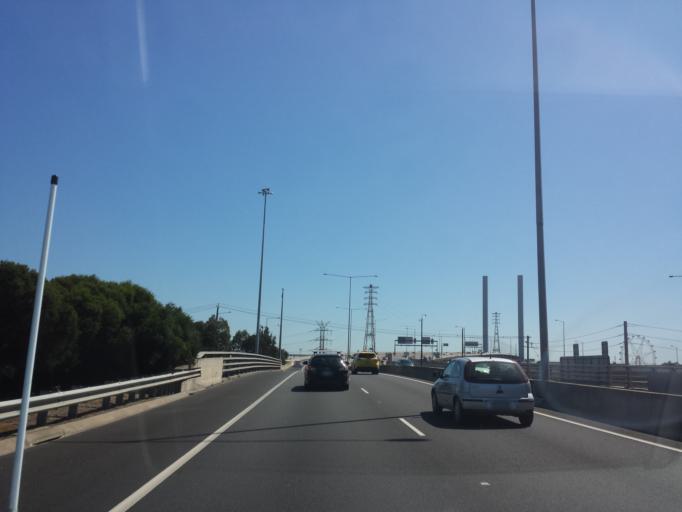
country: AU
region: Victoria
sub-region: Port Phillip
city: Port Melbourne
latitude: -37.8271
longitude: 144.9308
